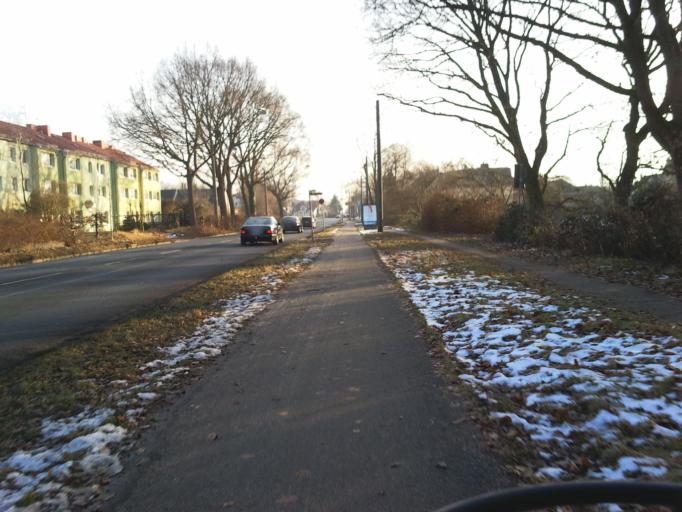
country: DE
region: Lower Saxony
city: Ritterhude
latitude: 53.1464
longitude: 8.7117
